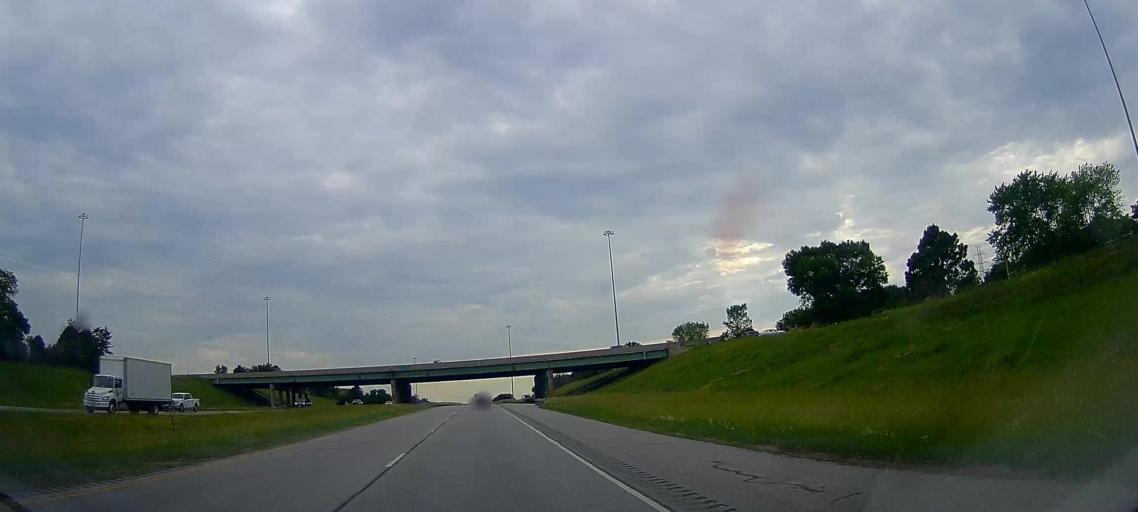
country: US
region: Iowa
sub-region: Pottawattamie County
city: Carter Lake
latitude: 41.3416
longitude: -96.0232
